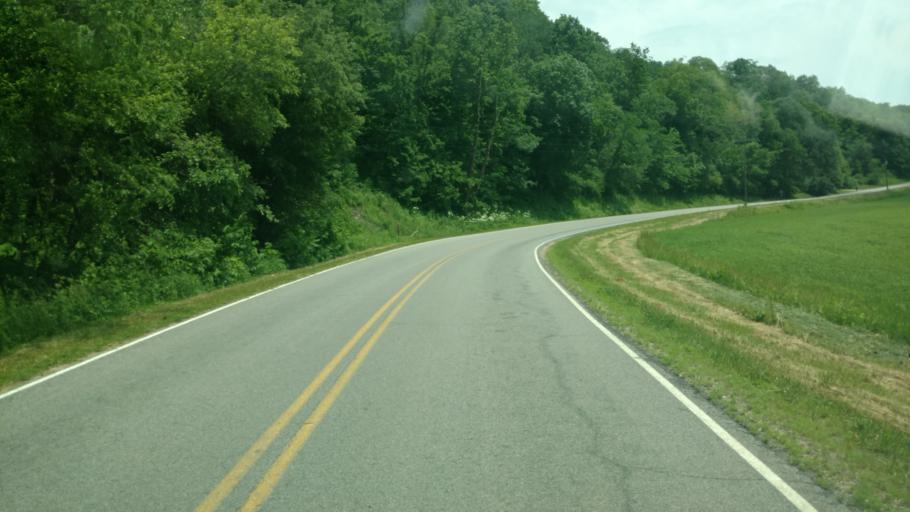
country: US
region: Wisconsin
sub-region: Monroe County
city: Cashton
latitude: 43.6604
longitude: -90.7137
